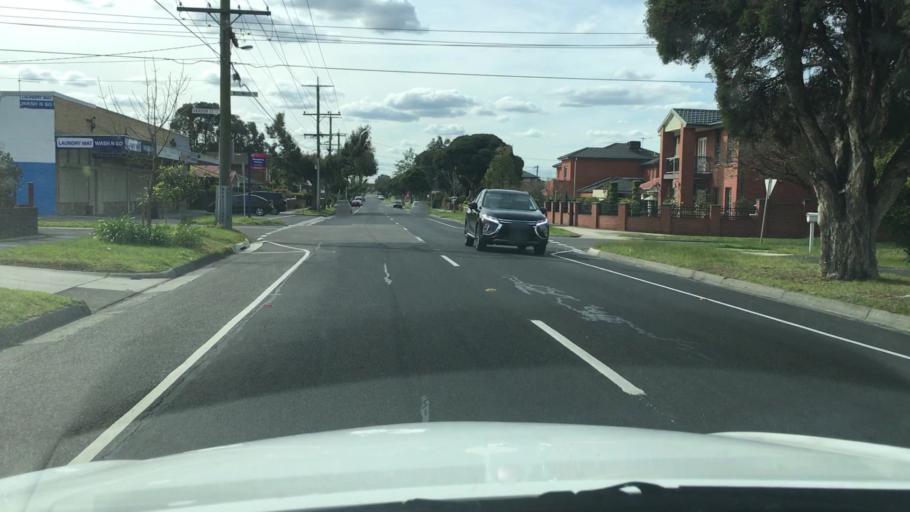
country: AU
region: Victoria
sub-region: Greater Dandenong
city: Springvale South
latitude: -37.9593
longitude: 145.1571
